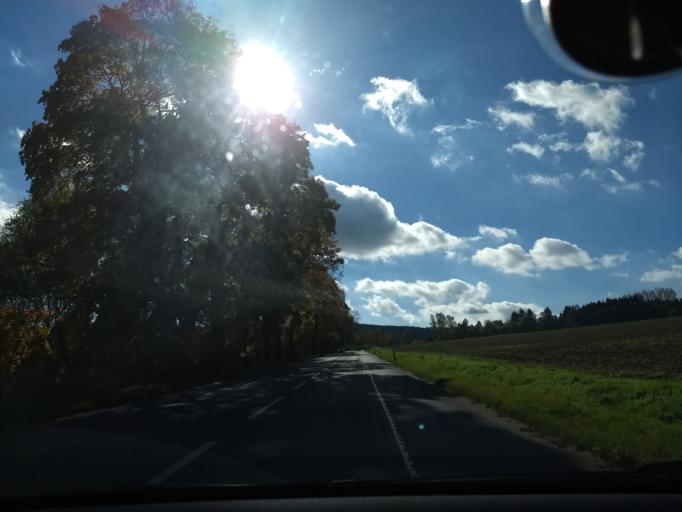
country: DE
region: North Rhine-Westphalia
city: Warstein
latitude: 51.4291
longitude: 8.3466
